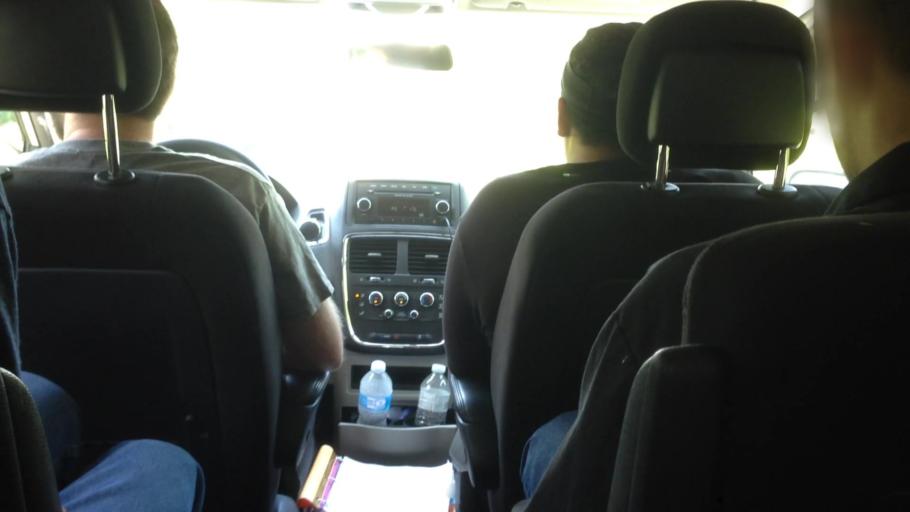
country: US
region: New York
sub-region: Dutchess County
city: Tivoli
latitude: 42.1158
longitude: -73.8913
